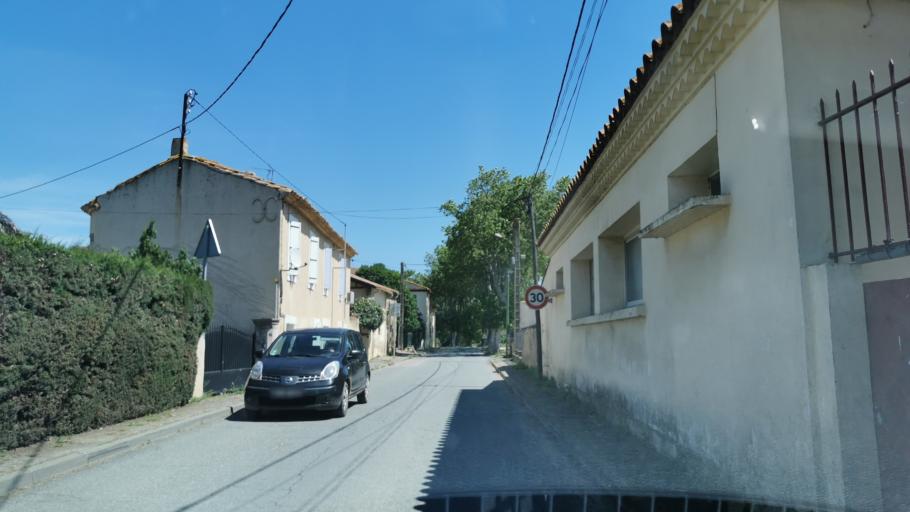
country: FR
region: Languedoc-Roussillon
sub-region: Departement de l'Aude
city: Canet
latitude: 43.2304
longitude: 2.8490
